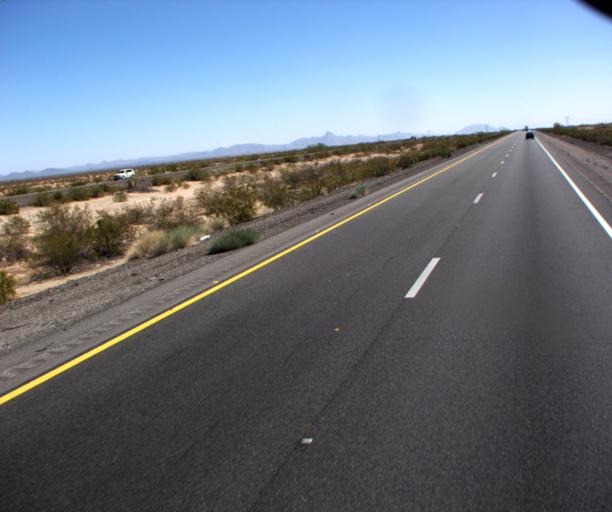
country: US
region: Arizona
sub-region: La Paz County
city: Salome
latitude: 33.5798
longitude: -113.4264
